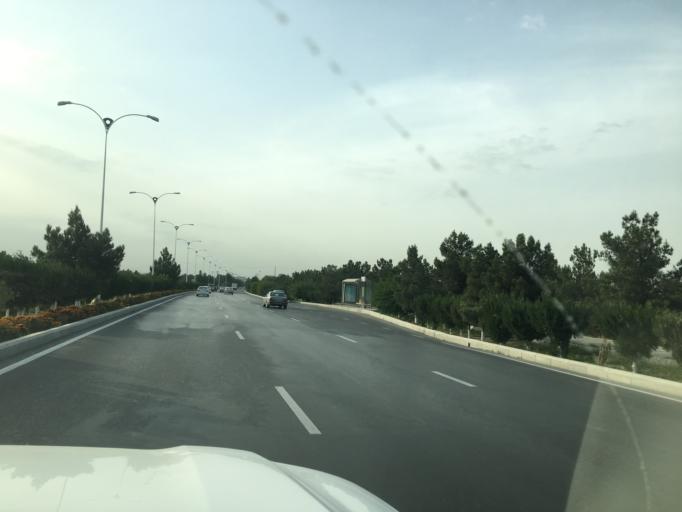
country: TM
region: Ahal
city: Annau
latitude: 37.9194
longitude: 58.4524
